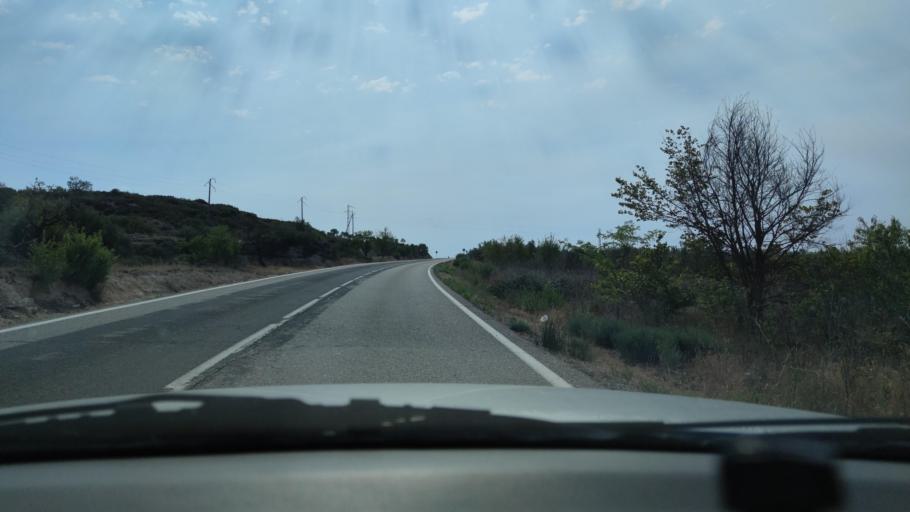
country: ES
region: Catalonia
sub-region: Provincia de Lleida
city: Arbeca
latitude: 41.5064
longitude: 0.9259
